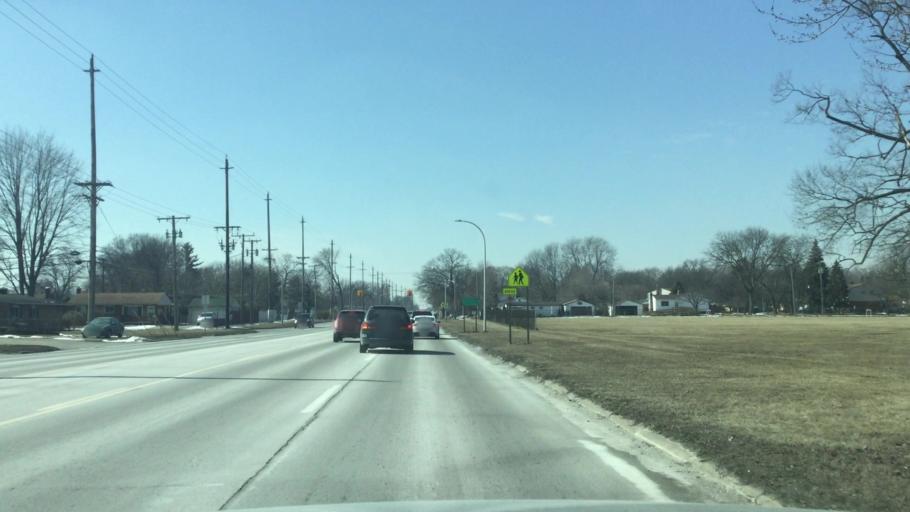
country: US
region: Michigan
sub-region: Wayne County
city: Westland
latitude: 42.3102
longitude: -83.3767
